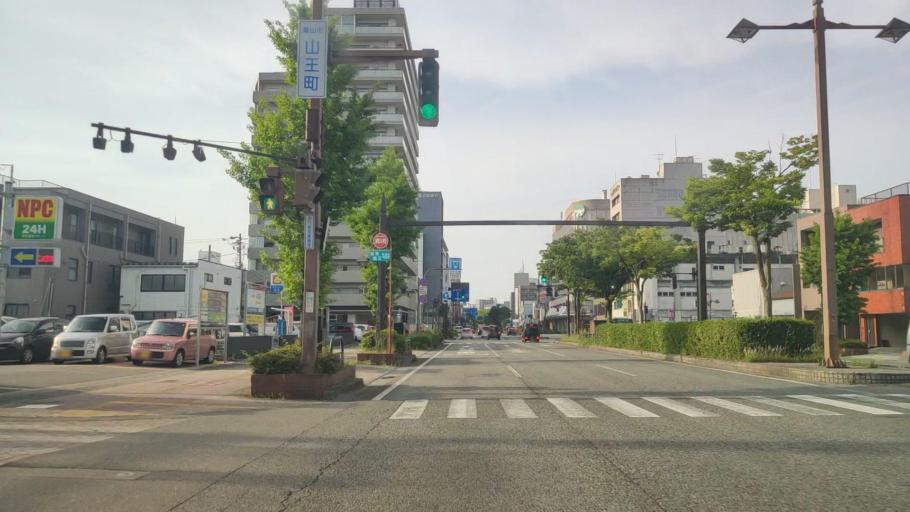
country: JP
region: Toyama
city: Toyama-shi
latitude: 36.6873
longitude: 137.2121
